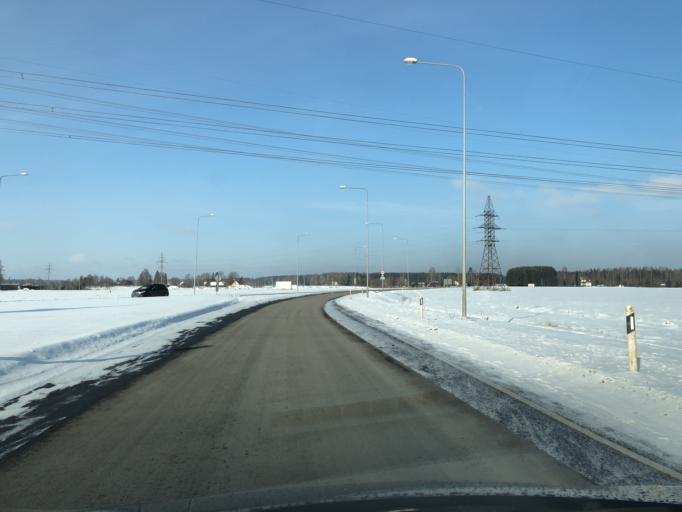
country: EE
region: Tartu
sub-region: Tartu linn
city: Tartu
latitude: 58.3795
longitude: 26.6762
